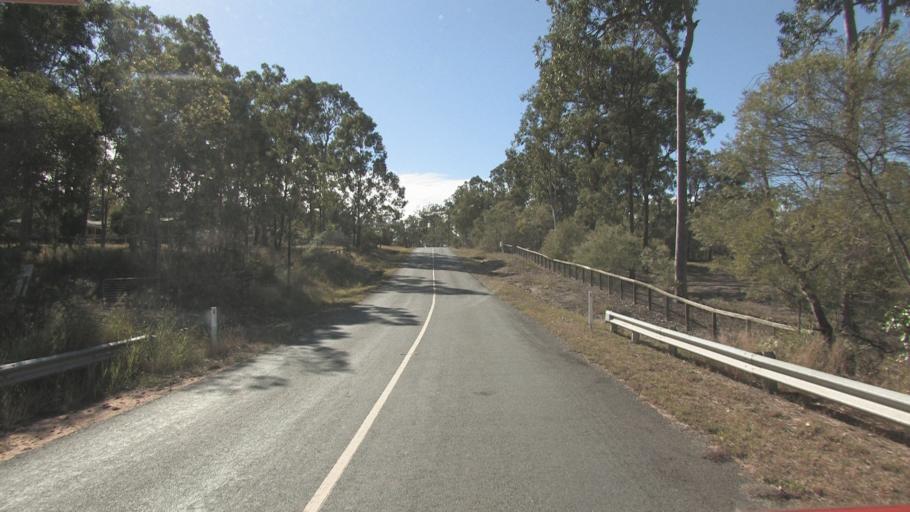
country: AU
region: Queensland
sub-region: Ipswich
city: Springfield Lakes
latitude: -27.7121
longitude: 152.9199
